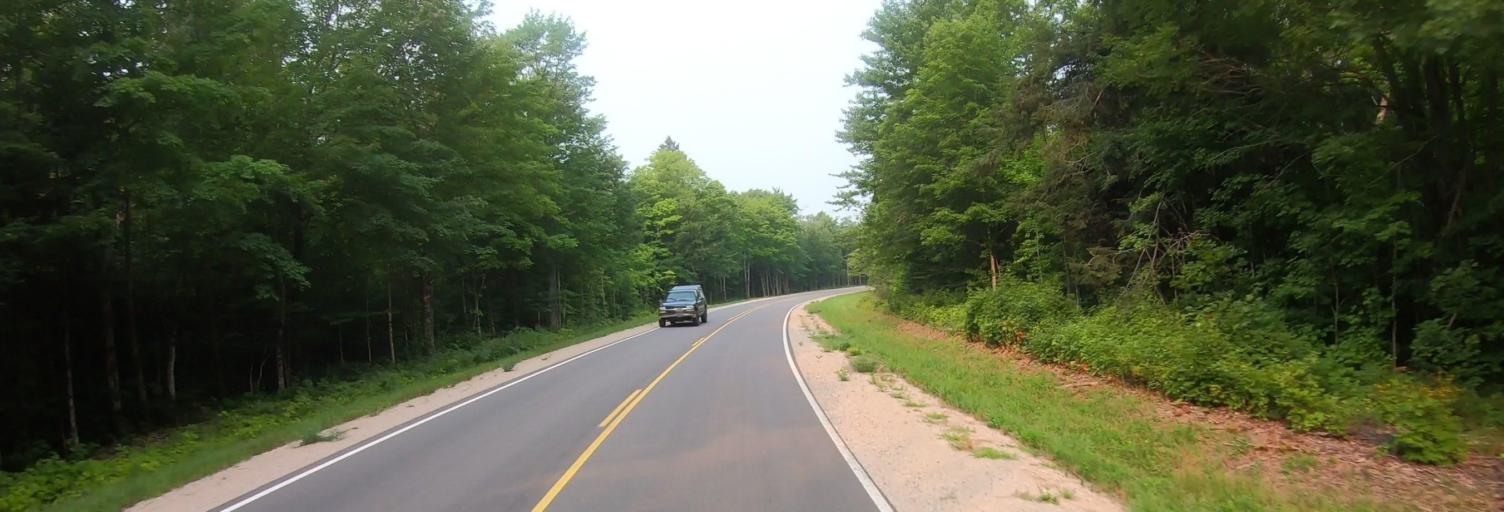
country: US
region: Michigan
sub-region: Luce County
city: Newberry
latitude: 46.4849
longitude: -85.0942
